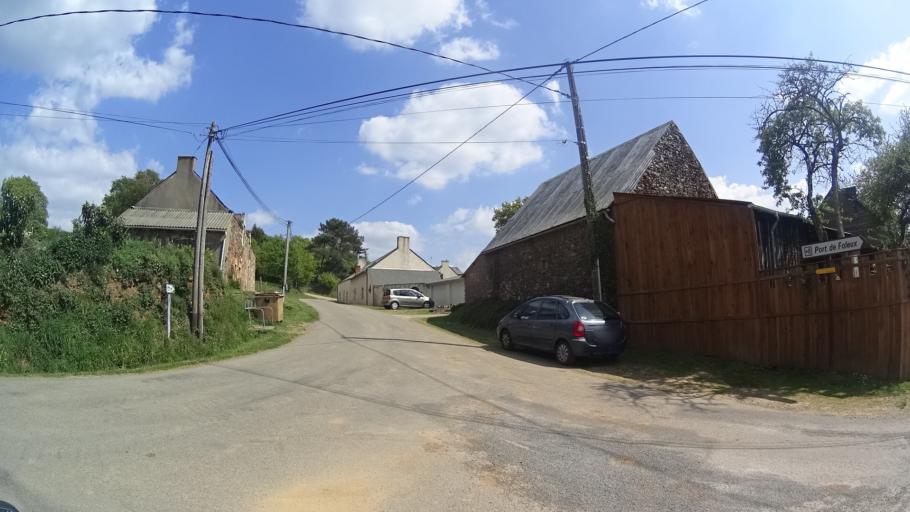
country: FR
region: Brittany
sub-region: Departement du Morbihan
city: Beganne
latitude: 47.5794
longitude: -2.2835
